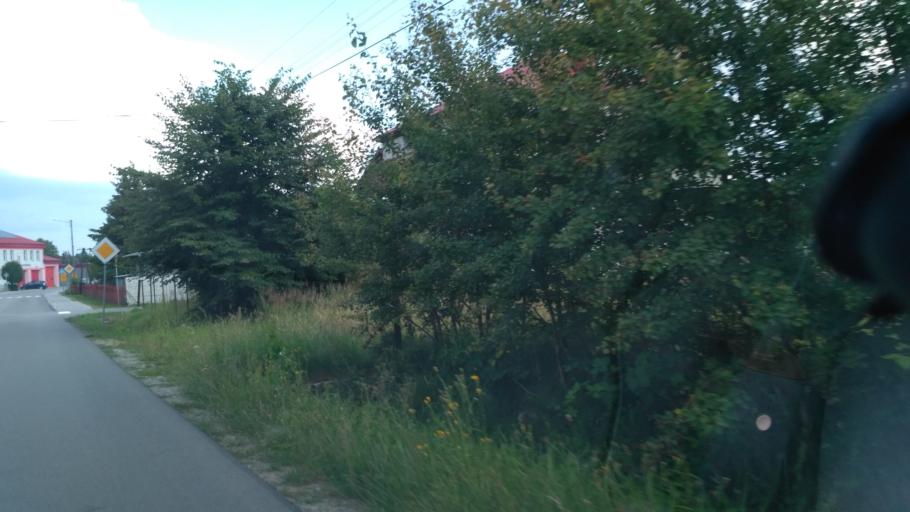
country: PL
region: Subcarpathian Voivodeship
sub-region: Powiat rzeszowski
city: Wysoka Glogowska
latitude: 50.1592
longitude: 22.0194
